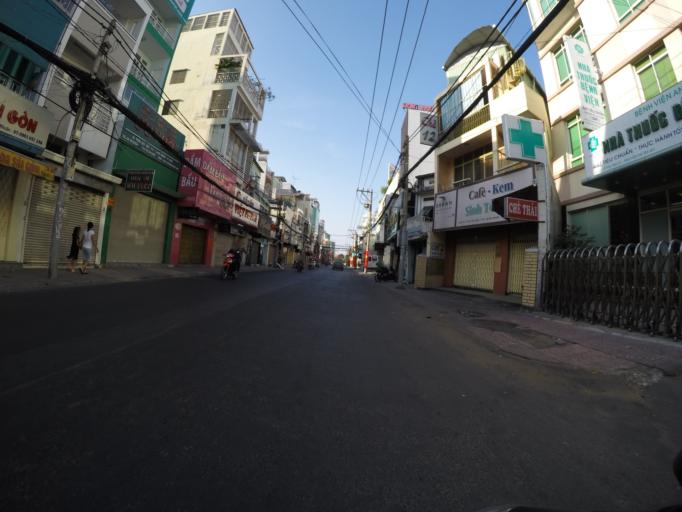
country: VN
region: Ho Chi Minh City
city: Quan Phu Nhuan
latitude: 10.7913
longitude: 106.6781
